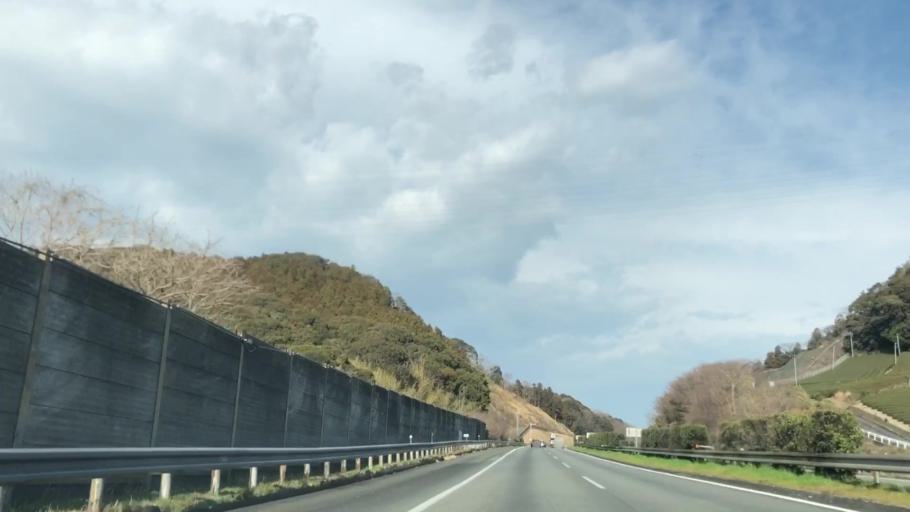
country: JP
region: Shizuoka
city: Shimada
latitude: 34.7607
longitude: 138.2030
